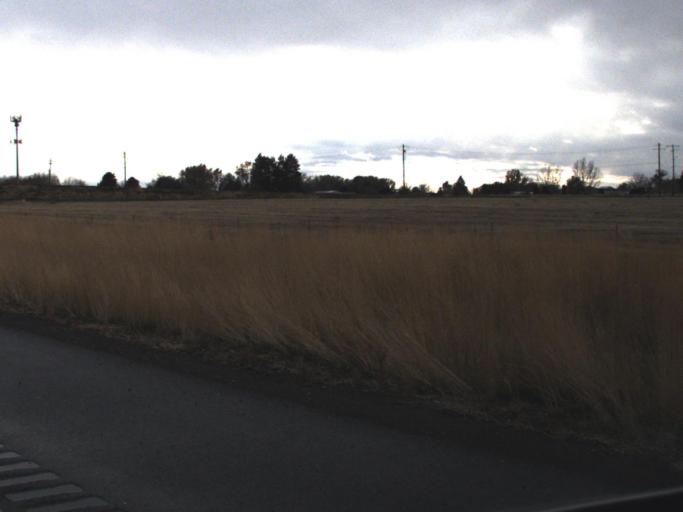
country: US
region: Washington
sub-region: Walla Walla County
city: Burbank
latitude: 46.1993
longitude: -118.9990
